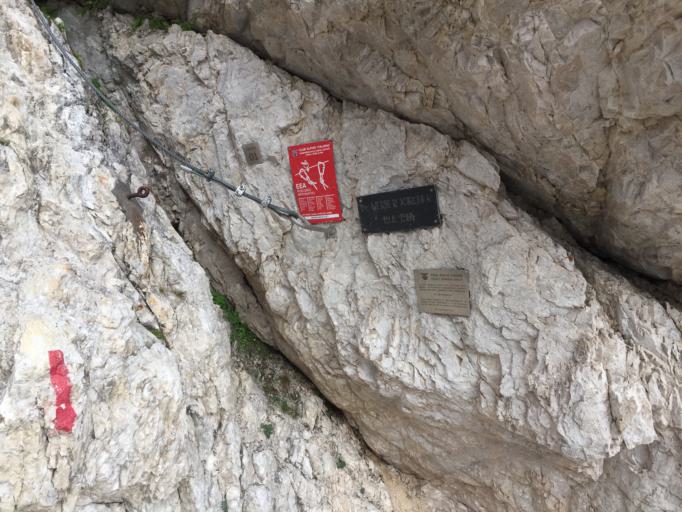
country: IT
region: Friuli Venezia Giulia
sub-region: Provincia di Udine
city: Malborghetto
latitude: 46.4275
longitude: 13.4963
